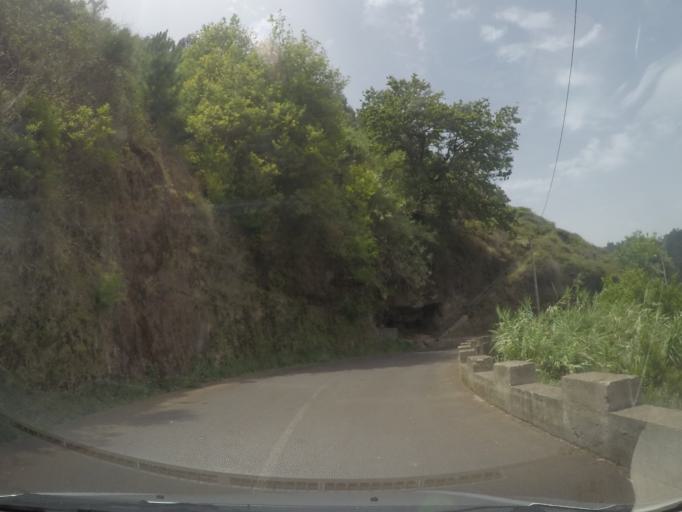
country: PT
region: Madeira
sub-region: Santa Cruz
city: Camacha
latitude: 32.6772
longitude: -16.8378
